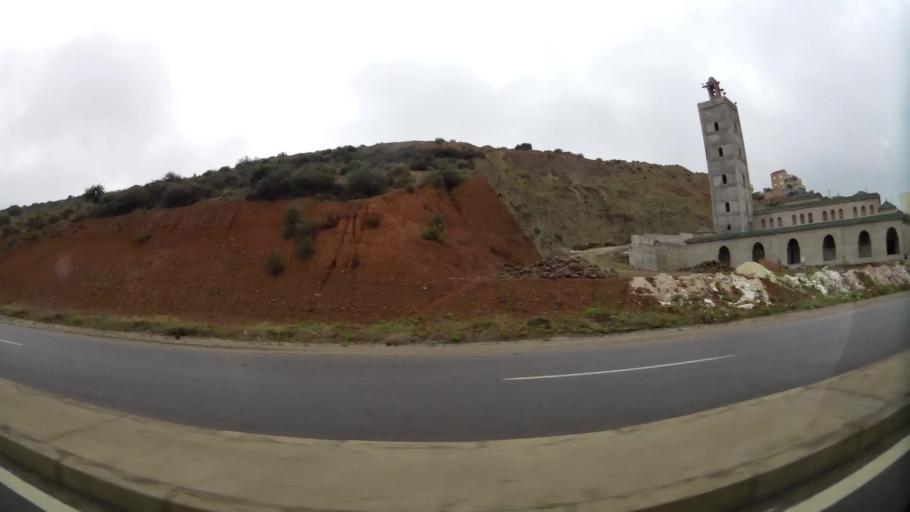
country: MA
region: Taza-Al Hoceima-Taounate
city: Imzourene
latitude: 35.1909
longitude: -3.8881
